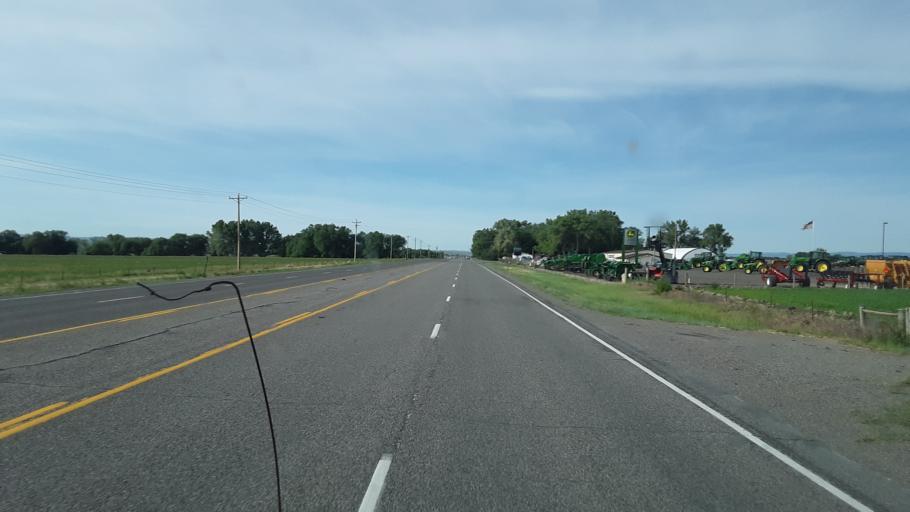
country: US
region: Wyoming
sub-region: Fremont County
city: Riverton
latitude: 43.0686
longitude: -108.3811
